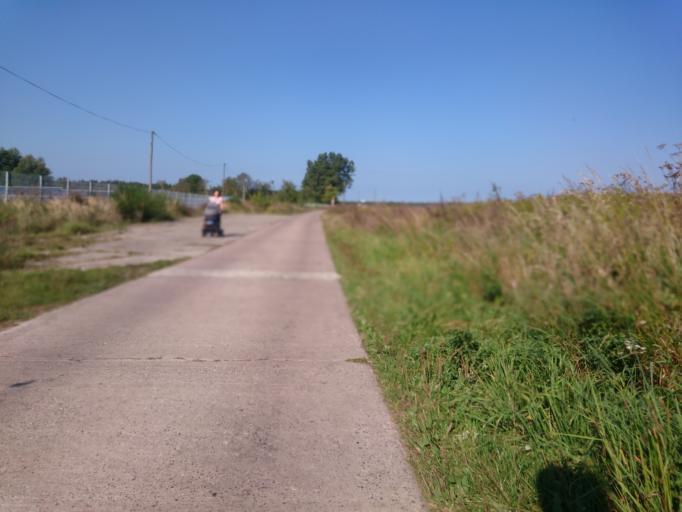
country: DE
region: Mecklenburg-Vorpommern
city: Barth
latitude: 54.3734
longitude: 12.6982
